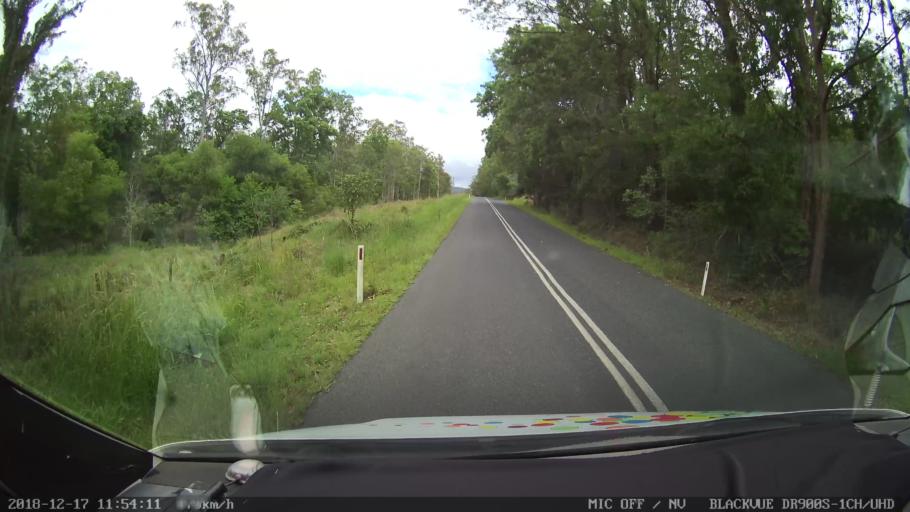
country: AU
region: New South Wales
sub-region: Kyogle
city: Kyogle
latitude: -28.5687
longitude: 152.5843
